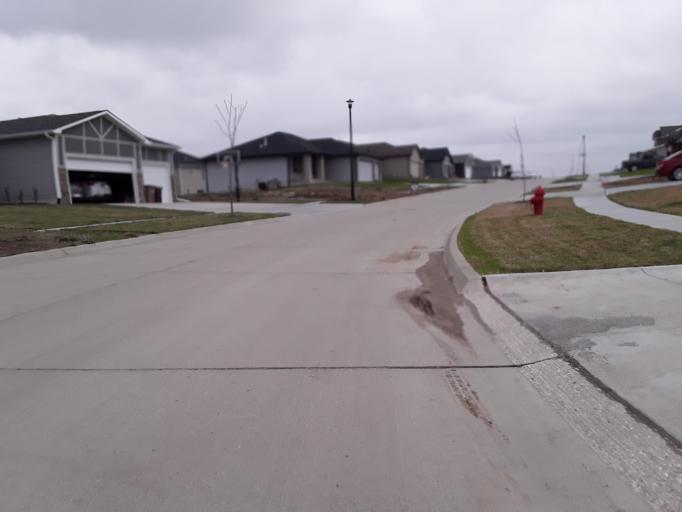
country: US
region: Nebraska
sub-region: Lancaster County
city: Lincoln
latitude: 40.8434
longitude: -96.5953
